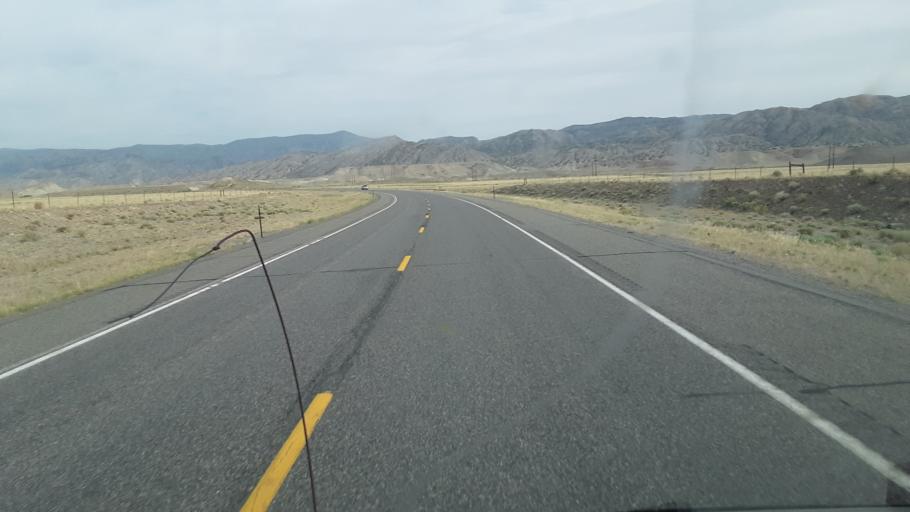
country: US
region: Wyoming
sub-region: Hot Springs County
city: Thermopolis
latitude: 43.3647
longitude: -108.1158
